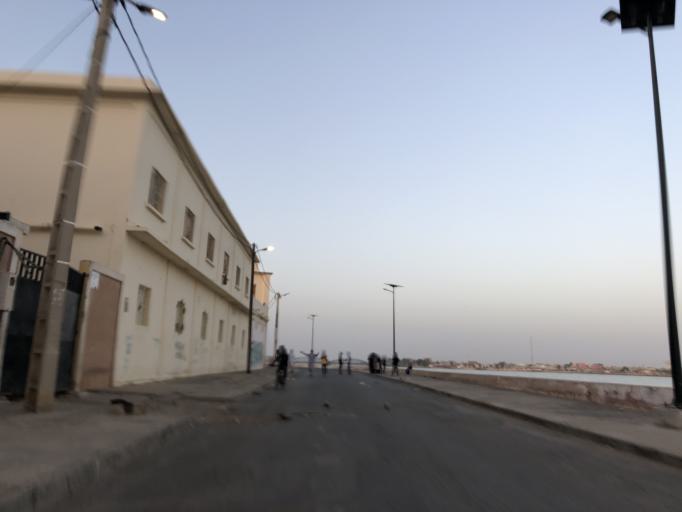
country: SN
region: Saint-Louis
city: Saint-Louis
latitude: 16.0187
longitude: -16.5052
